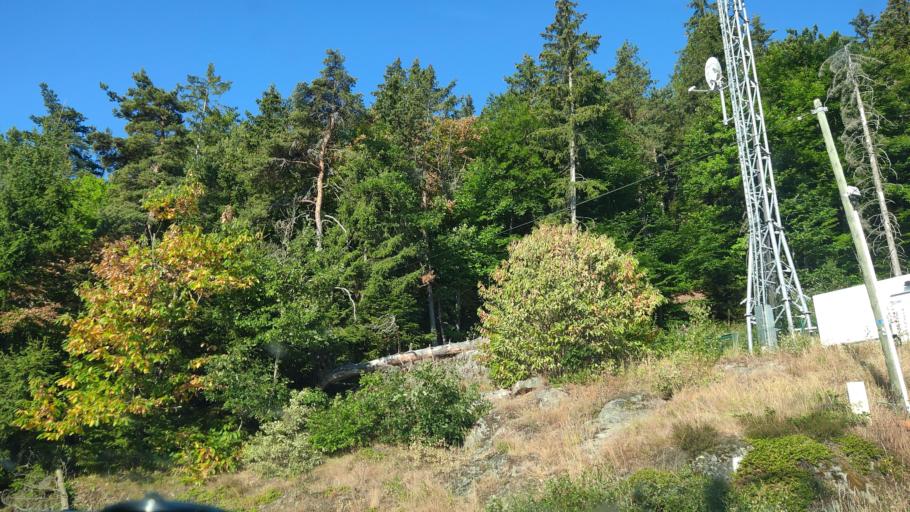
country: FR
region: Rhone-Alpes
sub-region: Departement de la Savoie
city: Saint-Etienne-de-Cuines
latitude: 45.3514
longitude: 6.2761
